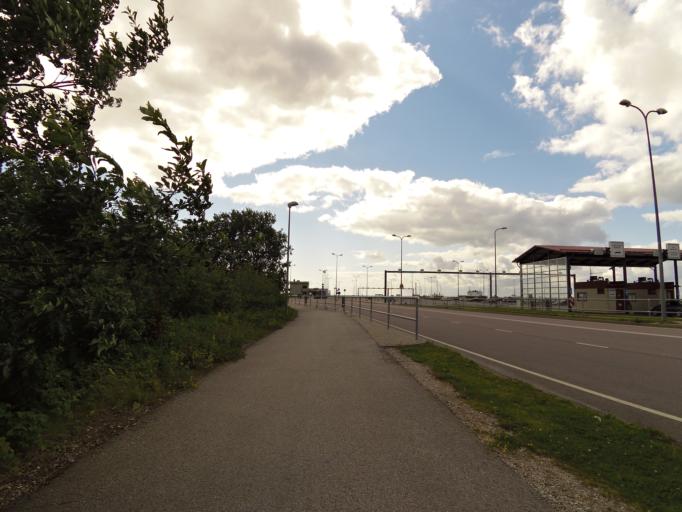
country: EE
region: Laeaene
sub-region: Haapsalu linn
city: Haapsalu
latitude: 58.9075
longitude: 23.4275
